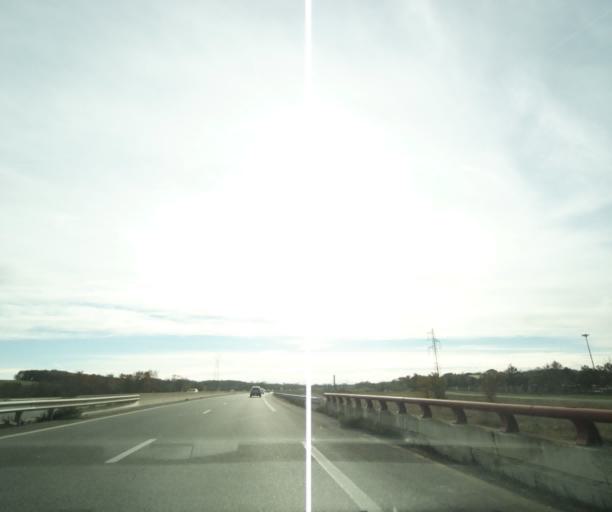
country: FR
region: Midi-Pyrenees
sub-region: Departement de la Haute-Garonne
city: La Salvetat-Saint-Gilles
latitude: 43.5958
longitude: 1.2776
